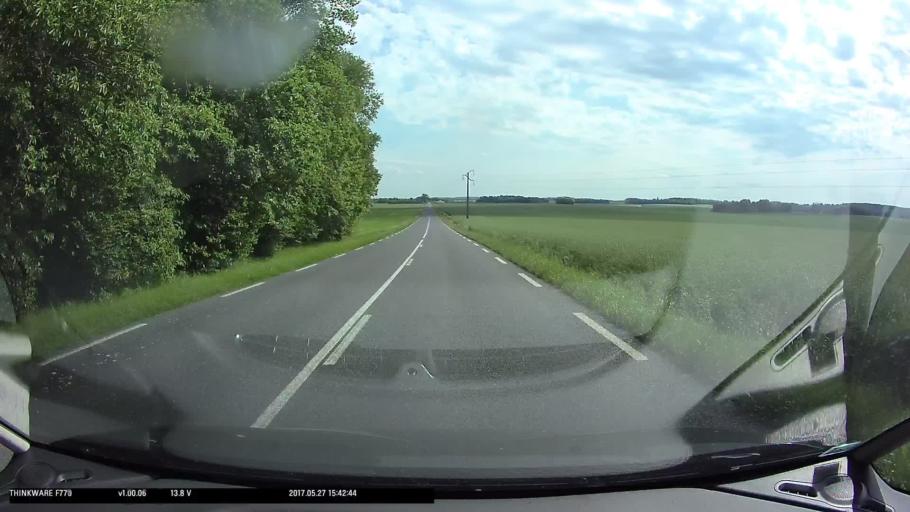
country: FR
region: Picardie
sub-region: Departement de l'Oise
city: Chaumont-en-Vexin
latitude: 49.2136
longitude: 1.8817
